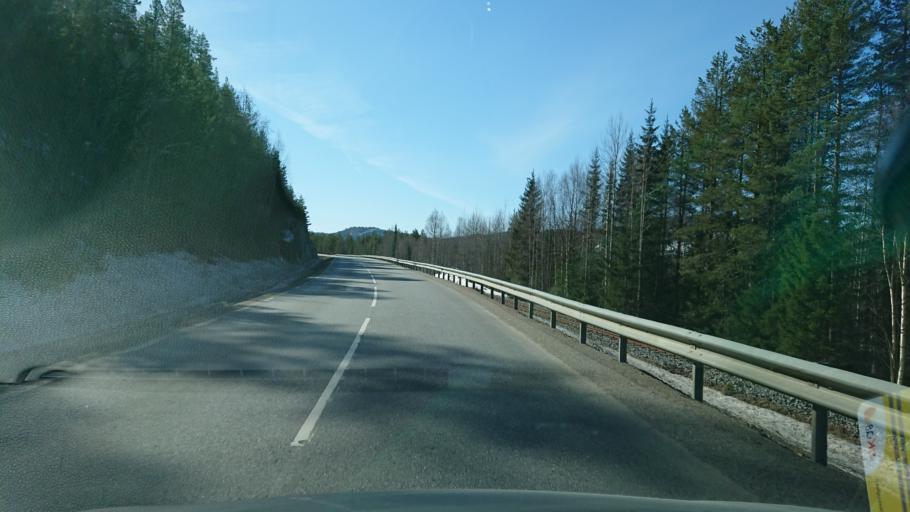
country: SE
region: Vaesterbotten
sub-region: Dorotea Kommun
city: Dorotea
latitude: 64.0529
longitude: 16.2589
